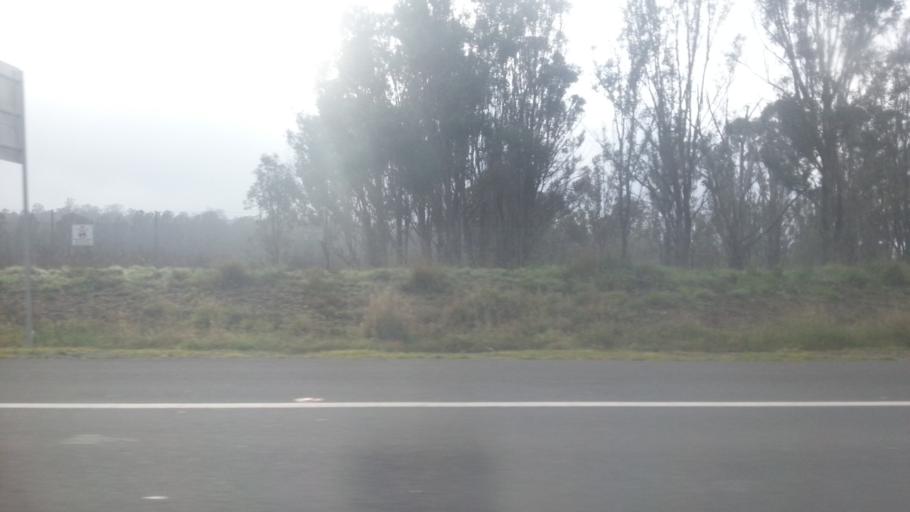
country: AU
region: New South Wales
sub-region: Penrith Municipality
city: Glenmore Park
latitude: -33.8033
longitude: 150.6968
